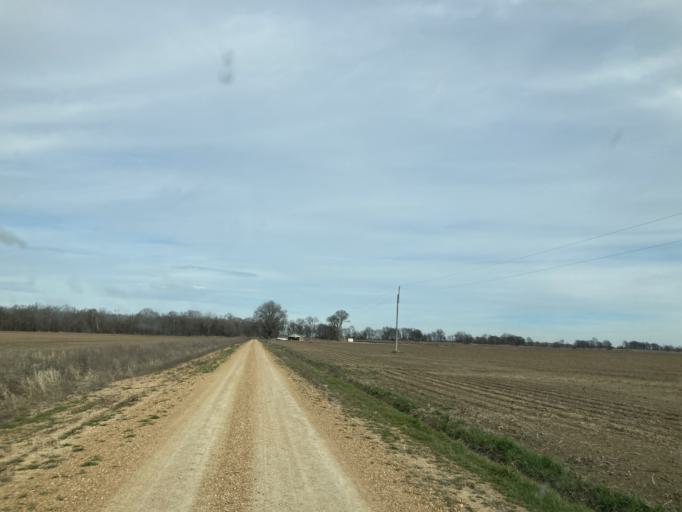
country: US
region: Mississippi
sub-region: Humphreys County
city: Belzoni
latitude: 33.0632
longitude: -90.6577
